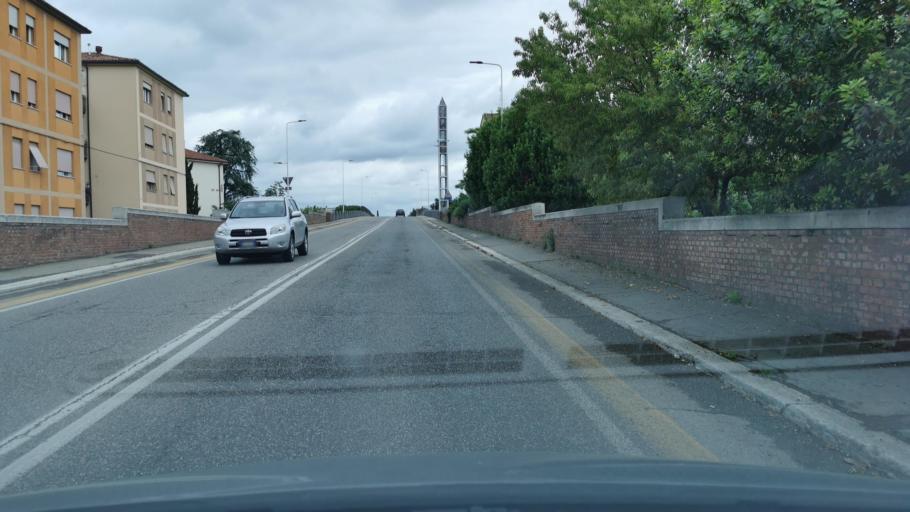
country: IT
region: Emilia-Romagna
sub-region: Provincia di Ravenna
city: Faenza
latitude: 44.2911
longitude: 11.8854
